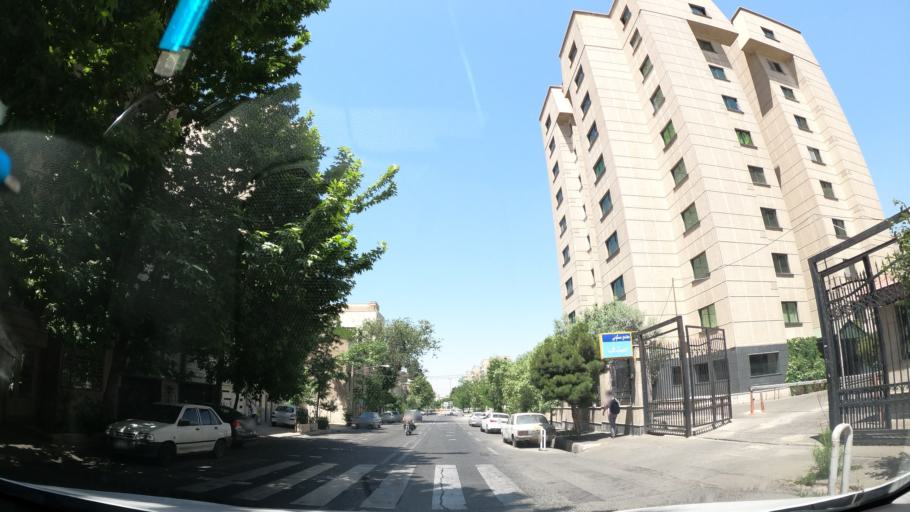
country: IR
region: Tehran
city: Tehran
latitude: 35.7256
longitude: 51.3669
